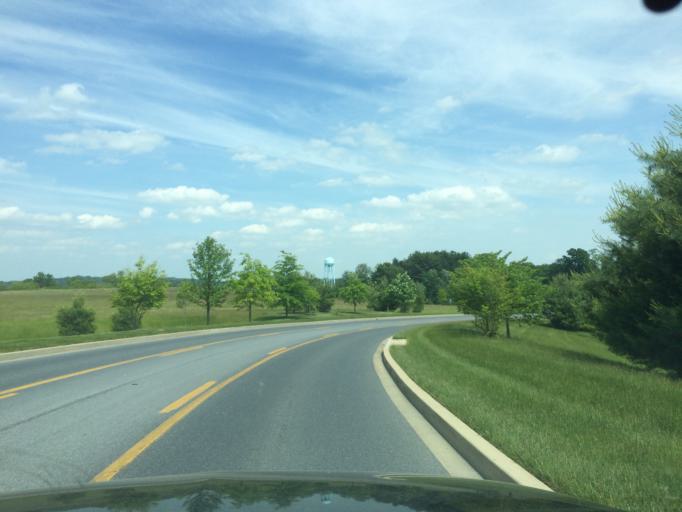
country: US
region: Maryland
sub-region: Carroll County
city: Sykesville
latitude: 39.3763
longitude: -76.9709
